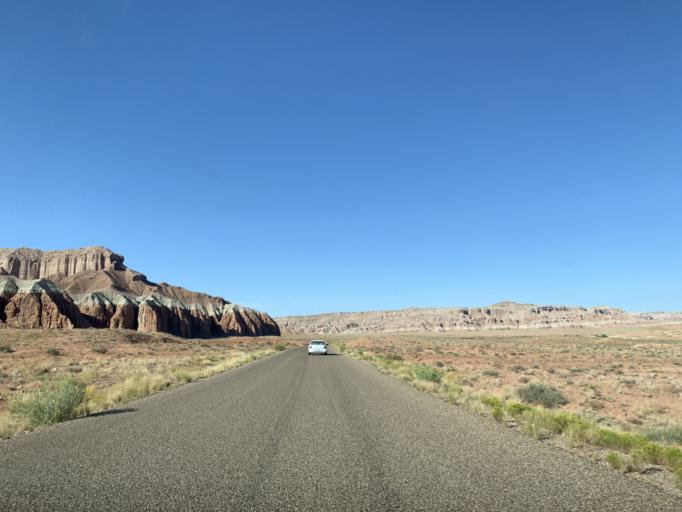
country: US
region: Utah
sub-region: Emery County
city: Ferron
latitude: 38.5821
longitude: -110.7245
